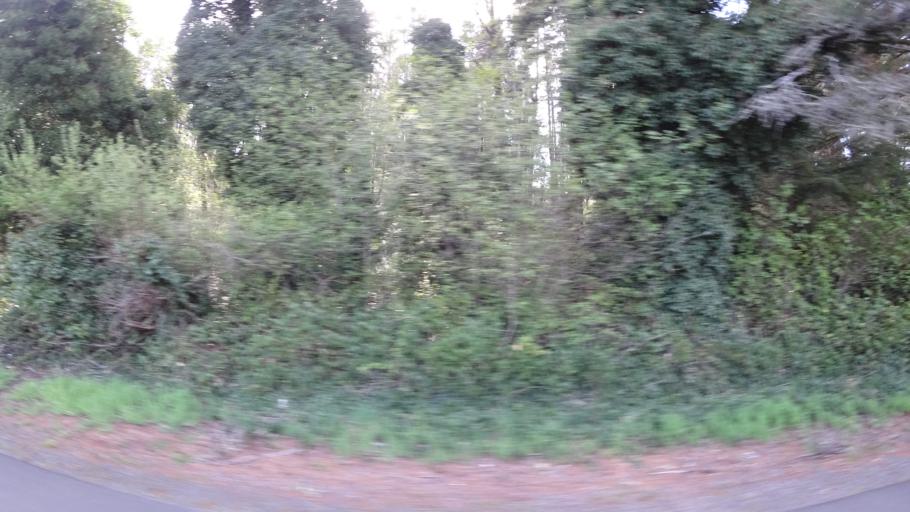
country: US
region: Oregon
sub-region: Lane County
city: Dunes City
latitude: 43.9085
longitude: -124.1123
